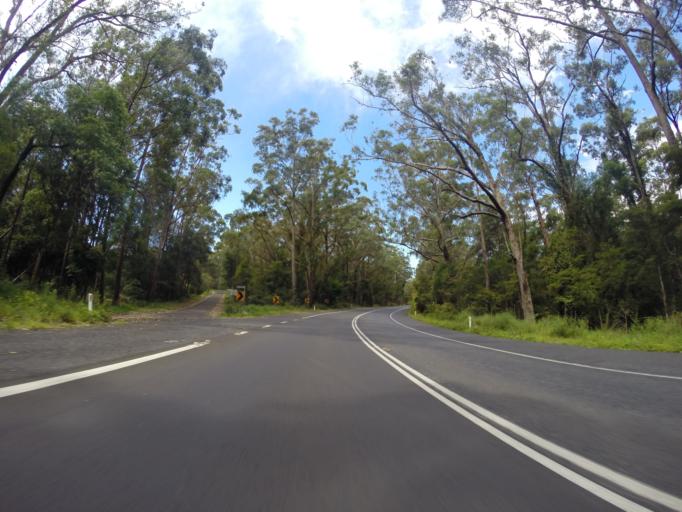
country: AU
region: New South Wales
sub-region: Shoalhaven Shire
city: Falls Creek
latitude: -35.0796
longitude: 150.5499
